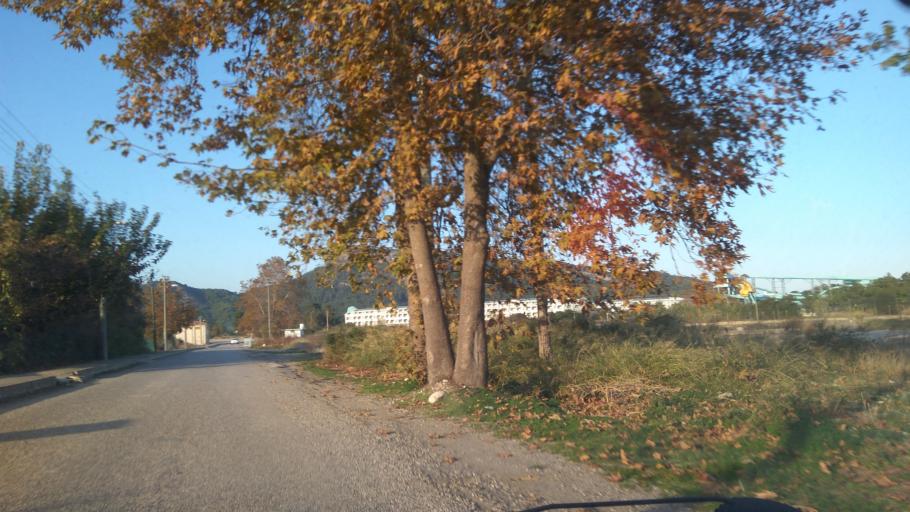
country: TR
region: Antalya
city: Kemer
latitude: 36.5623
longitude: 30.5716
